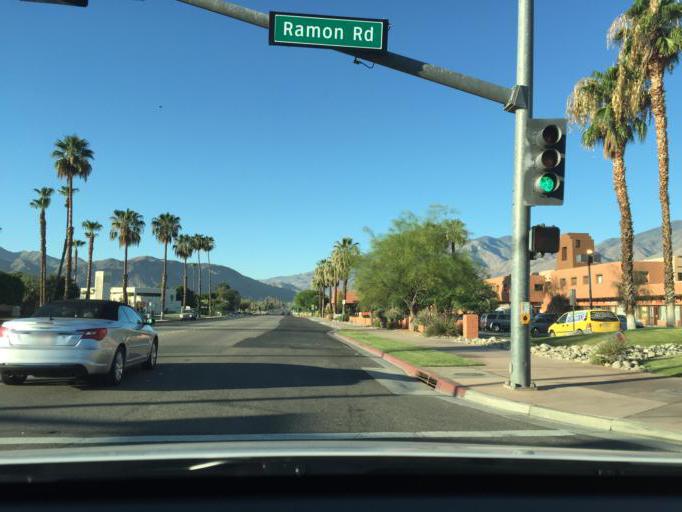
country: US
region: California
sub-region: Riverside County
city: Palm Springs
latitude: 33.8160
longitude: -116.5283
